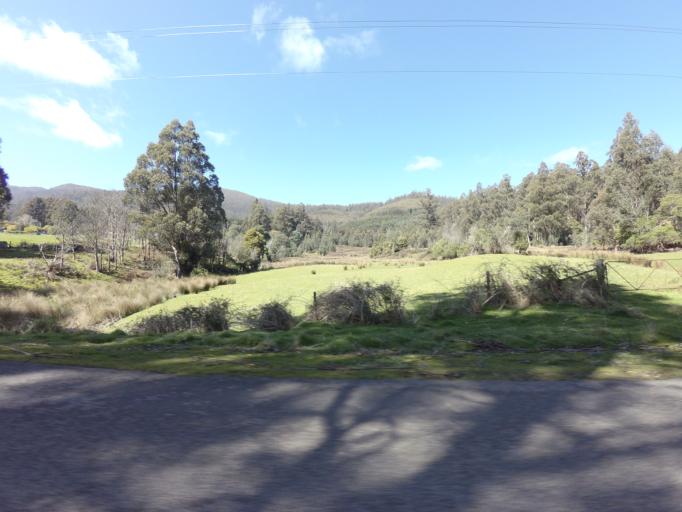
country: AU
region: Tasmania
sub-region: Derwent Valley
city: New Norfolk
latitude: -42.7571
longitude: 146.6208
